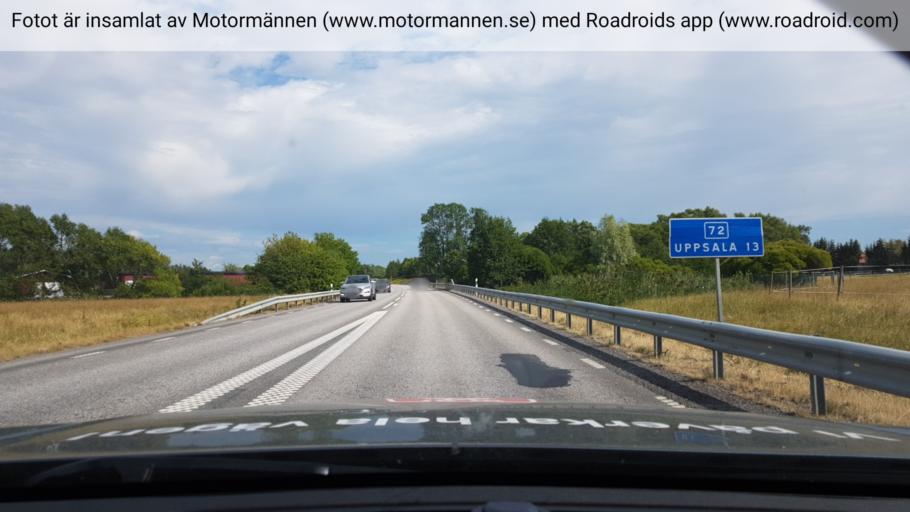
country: SE
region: Uppsala
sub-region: Enkopings Kommun
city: Orsundsbro
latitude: 59.8547
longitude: 17.4334
